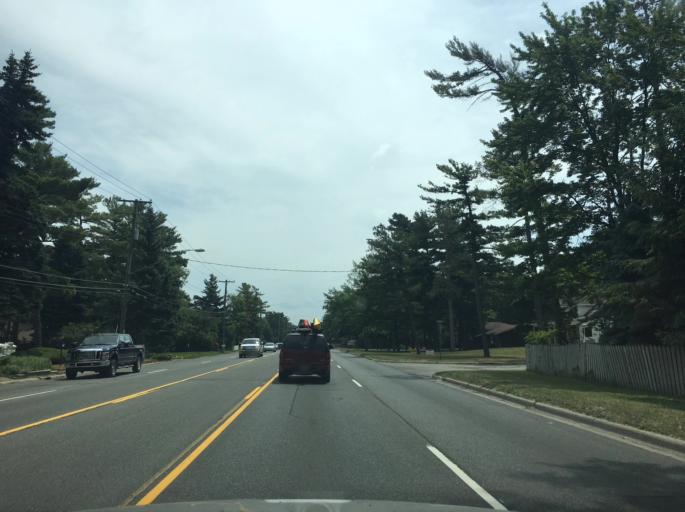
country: US
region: Michigan
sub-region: Grand Traverse County
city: Traverse City
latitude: 44.7542
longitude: -85.5712
